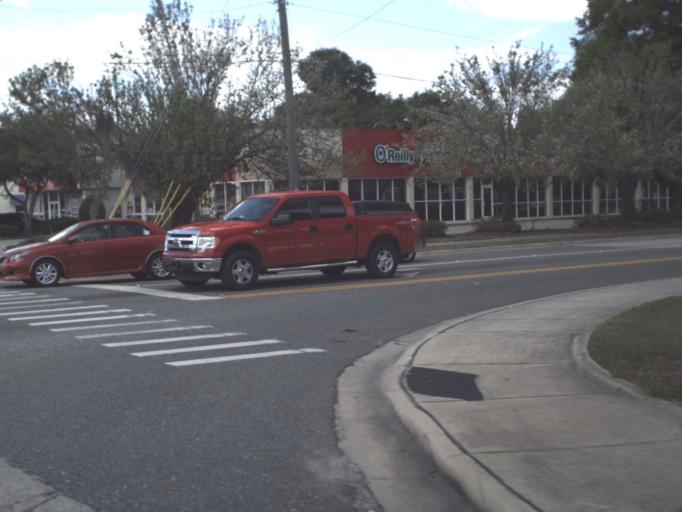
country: US
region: Florida
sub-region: Marion County
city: Ocala
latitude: 29.1695
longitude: -82.1648
